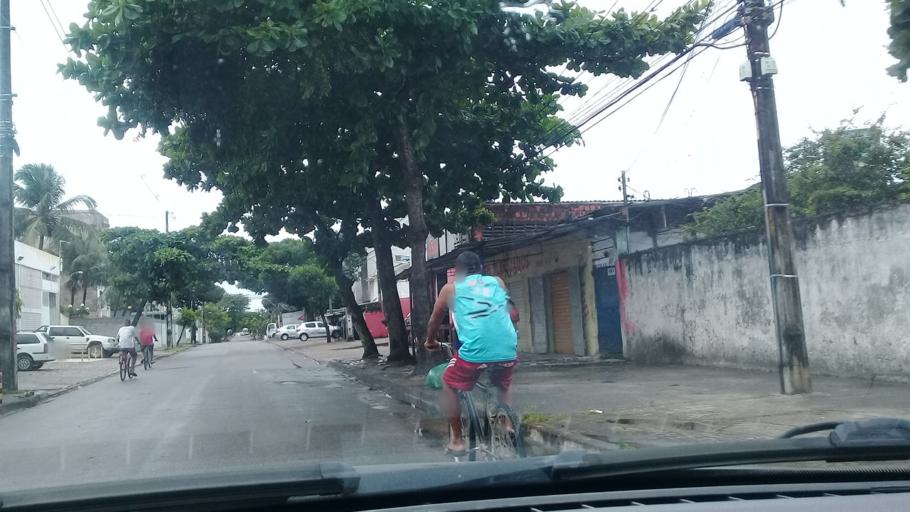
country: BR
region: Pernambuco
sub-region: Jaboatao Dos Guararapes
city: Jaboatao
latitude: -8.1430
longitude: -34.9154
